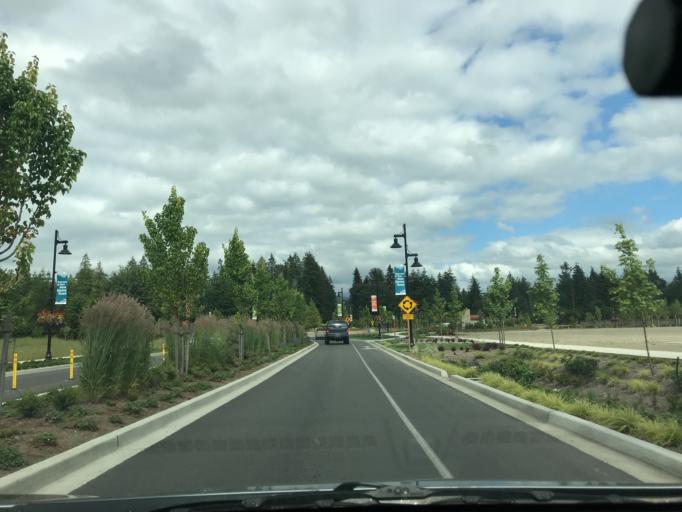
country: US
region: Washington
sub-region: King County
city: Black Diamond
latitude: 47.3113
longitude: -122.0318
